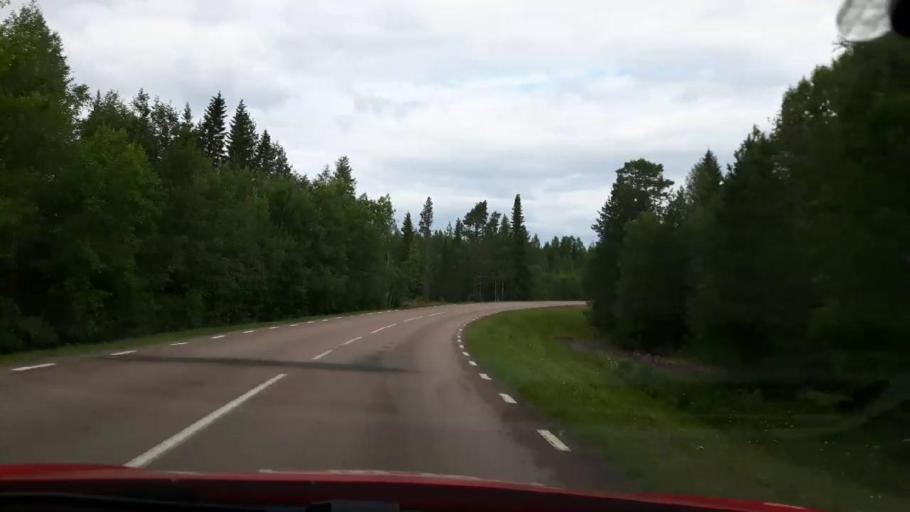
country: SE
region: Jaemtland
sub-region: Stroemsunds Kommun
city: Stroemsund
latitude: 63.8190
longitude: 15.6213
